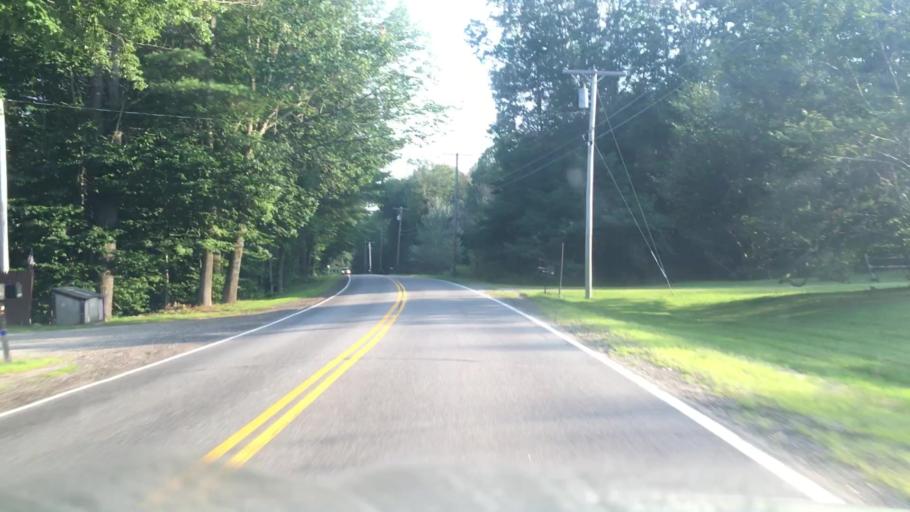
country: US
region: Maine
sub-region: Cumberland County
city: Freeport
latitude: 43.9237
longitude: -70.0906
